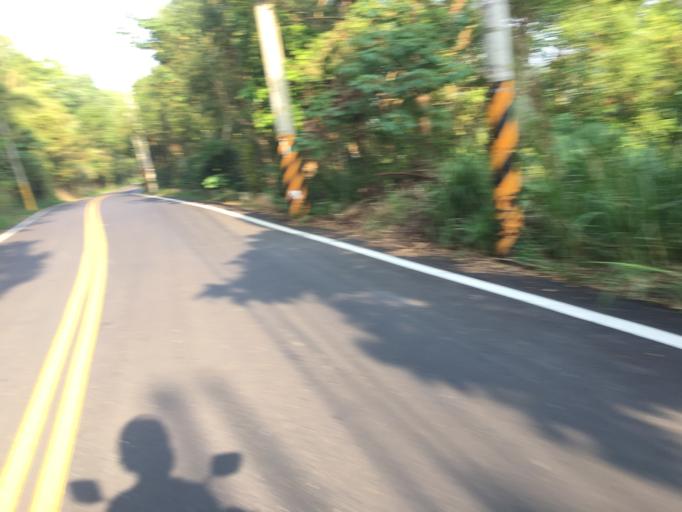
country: TW
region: Taiwan
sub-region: Hsinchu
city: Hsinchu
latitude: 24.7562
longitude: 121.0227
